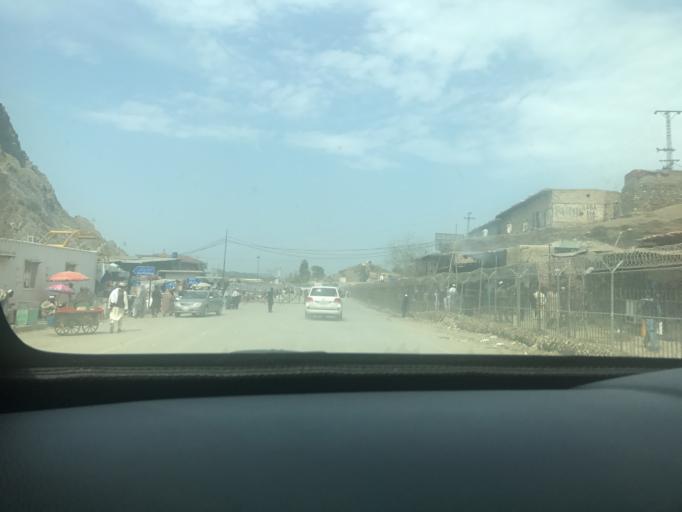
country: PK
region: Federally Administered Tribal Areas
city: Landi Kotal
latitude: 34.1191
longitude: 71.0987
